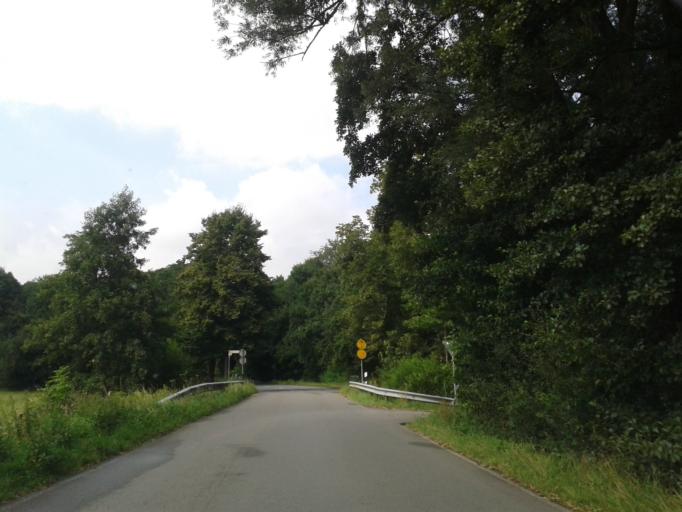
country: DE
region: North Rhine-Westphalia
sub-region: Regierungsbezirk Detmold
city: Blomberg
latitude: 51.9705
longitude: 9.0297
